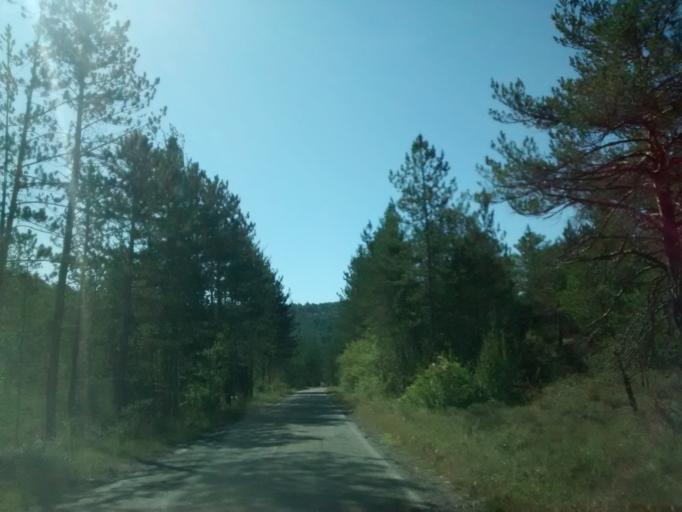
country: ES
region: Aragon
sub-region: Provincia de Huesca
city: Santa Cruz de la Seros
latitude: 42.4451
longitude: -0.6145
